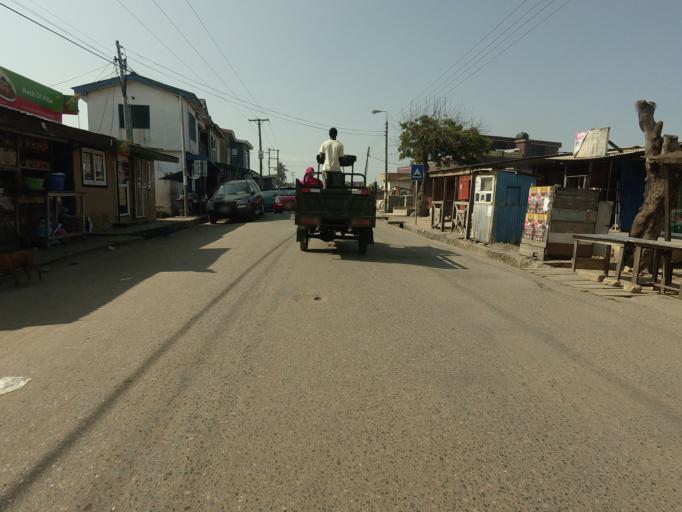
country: GH
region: Greater Accra
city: Teshi Old Town
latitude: 5.5823
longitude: -0.1008
